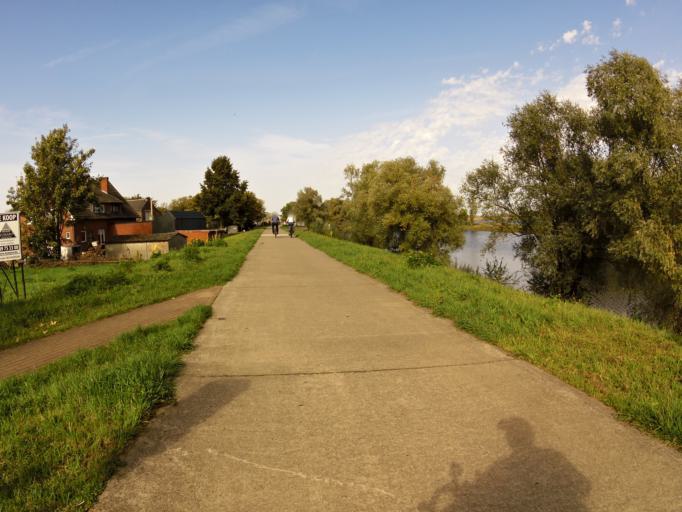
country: NL
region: Limburg
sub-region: Gemeente Stein
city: Berg
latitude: 51.0213
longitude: 5.7504
